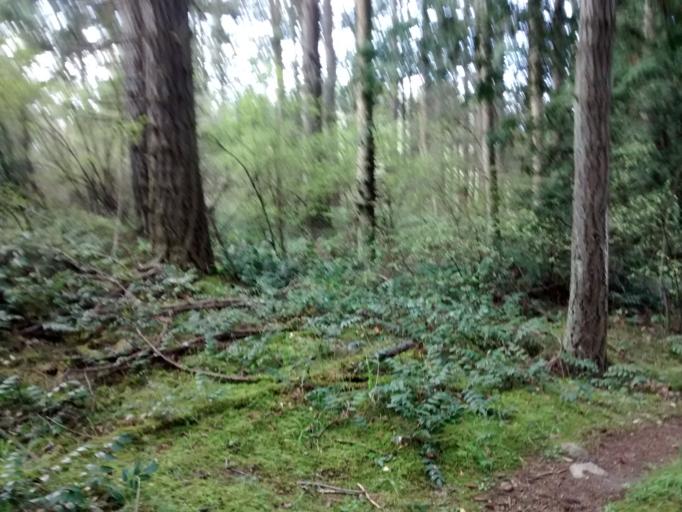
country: US
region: Washington
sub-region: Clallam County
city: Port Angeles
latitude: 48.1195
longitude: -123.4809
